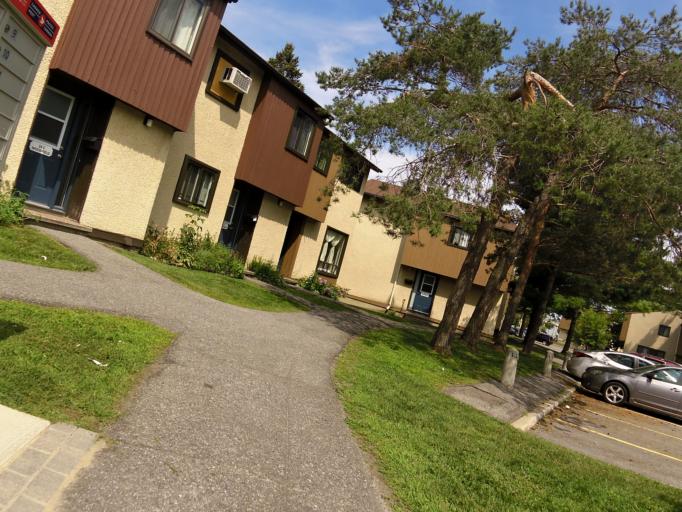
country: CA
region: Ontario
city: Ottawa
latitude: 45.3370
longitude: -75.7285
